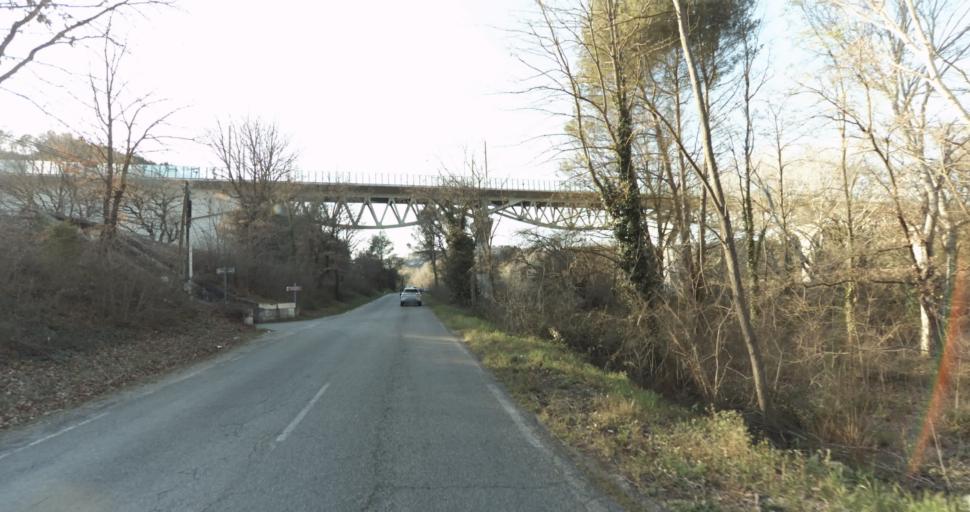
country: FR
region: Provence-Alpes-Cote d'Azur
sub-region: Departement des Bouches-du-Rhone
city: Ventabren
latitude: 43.5119
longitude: 5.3244
